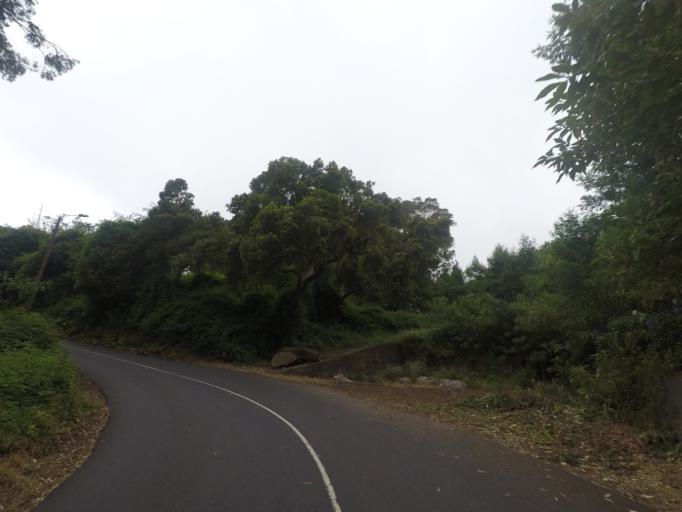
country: PT
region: Madeira
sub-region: Funchal
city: Nossa Senhora do Monte
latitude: 32.6669
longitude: -16.8768
